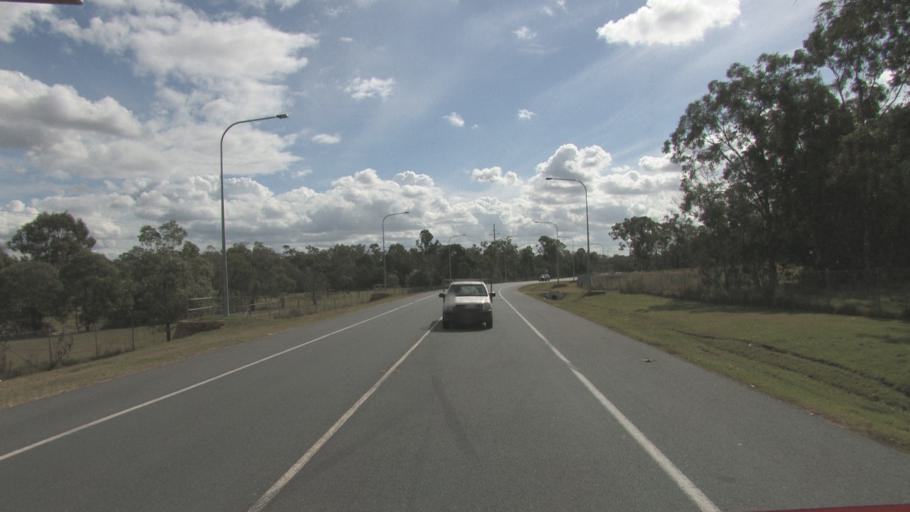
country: AU
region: Queensland
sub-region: Logan
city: Logan Reserve
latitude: -27.6916
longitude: 153.0701
